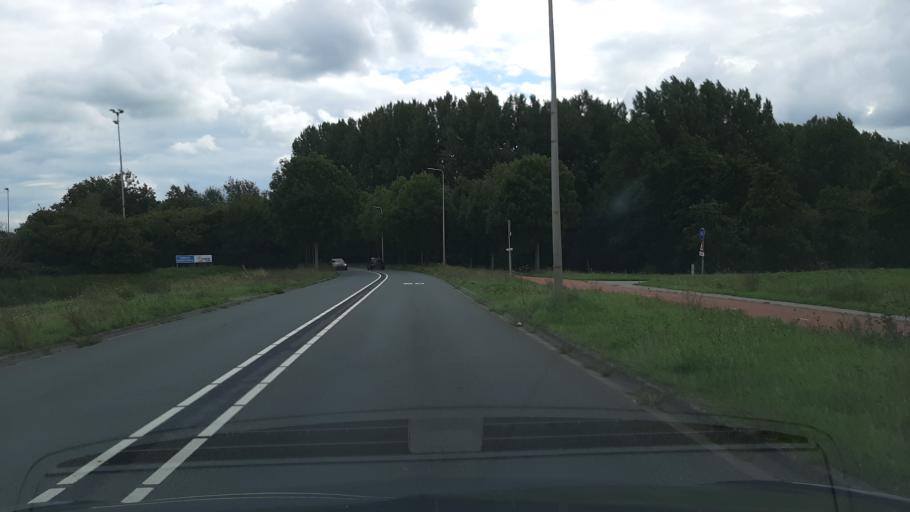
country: NL
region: Overijssel
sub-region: Gemeente Zwolle
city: Zwolle
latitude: 52.5347
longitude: 6.0766
